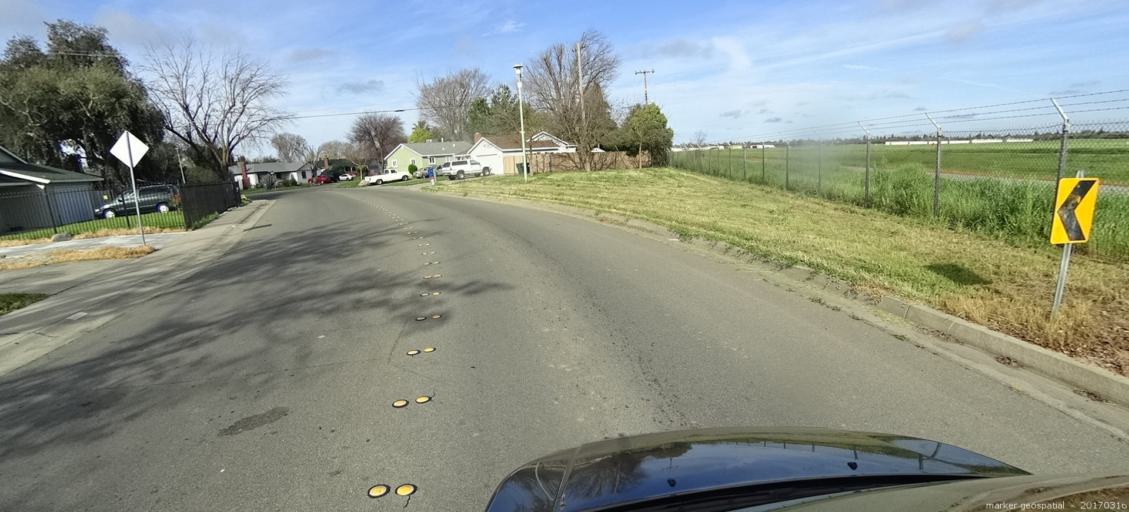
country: US
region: California
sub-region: Sacramento County
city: Parkway
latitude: 38.5103
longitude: -121.4870
